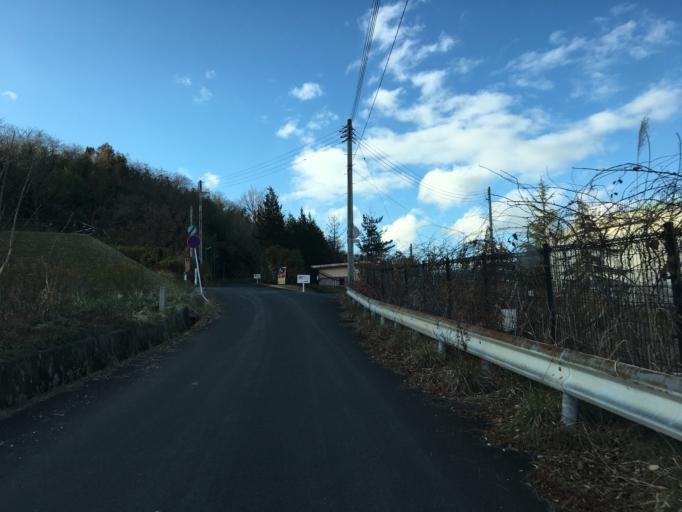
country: JP
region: Fukushima
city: Fukushima-shi
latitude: 37.8322
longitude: 140.4419
